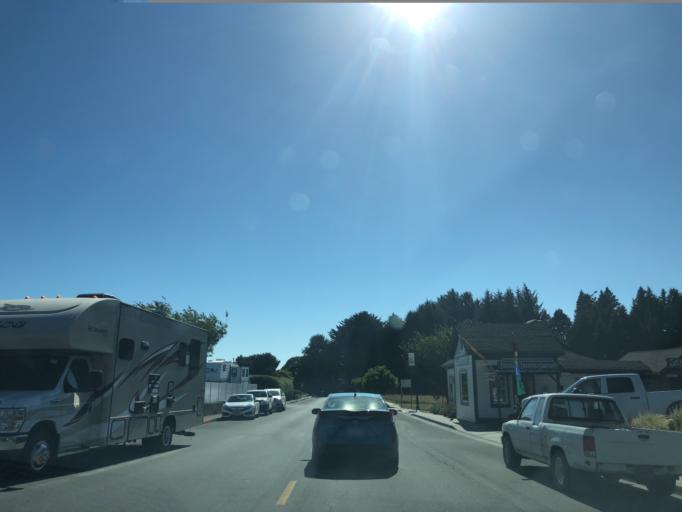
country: US
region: California
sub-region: Humboldt County
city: Westhaven-Moonstone
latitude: 41.0613
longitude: -124.1412
